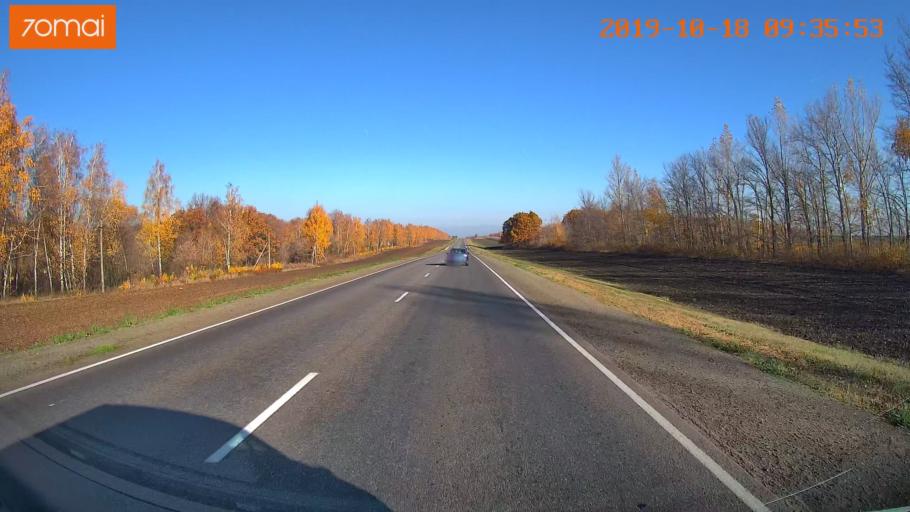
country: RU
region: Tula
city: Yefremov
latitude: 53.1982
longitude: 38.1471
